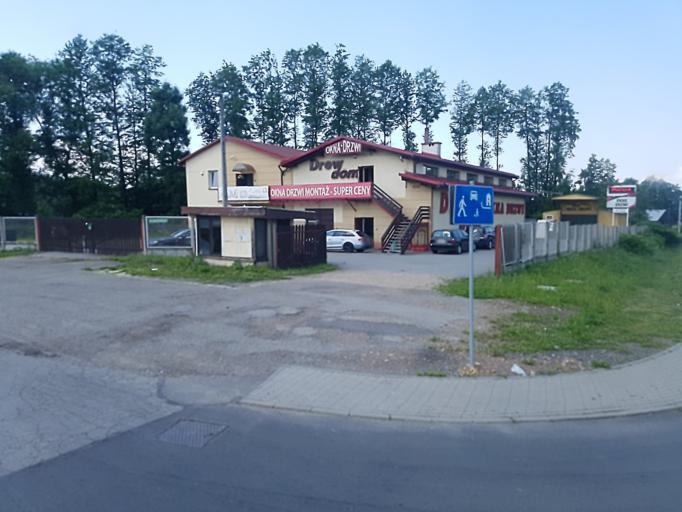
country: PL
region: Silesian Voivodeship
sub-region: Powiat bielski
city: Mazancowice
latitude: 49.8466
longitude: 18.9924
